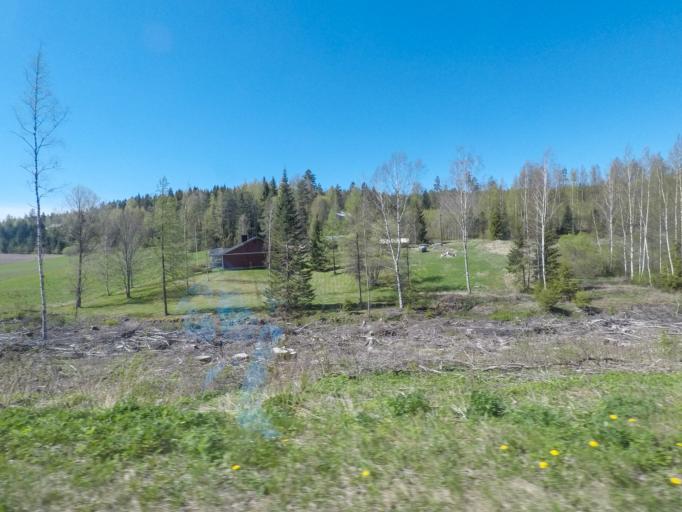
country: FI
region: Uusimaa
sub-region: Helsinki
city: Sammatti
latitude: 60.4075
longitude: 23.8196
